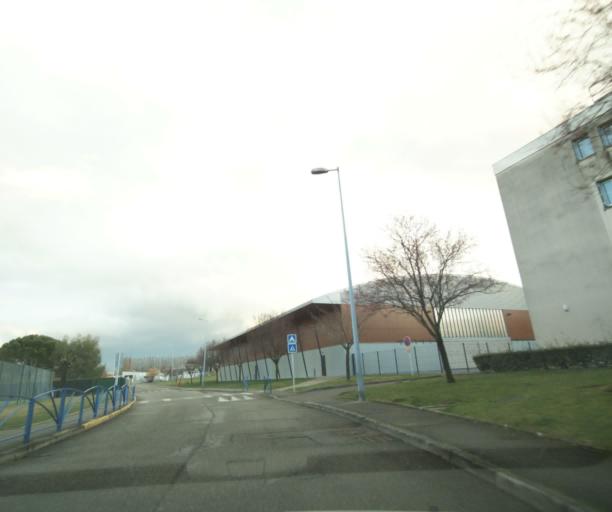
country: FR
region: Rhone-Alpes
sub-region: Departement de la Drome
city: Bourg-les-Valence
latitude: 44.9508
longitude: 4.9055
